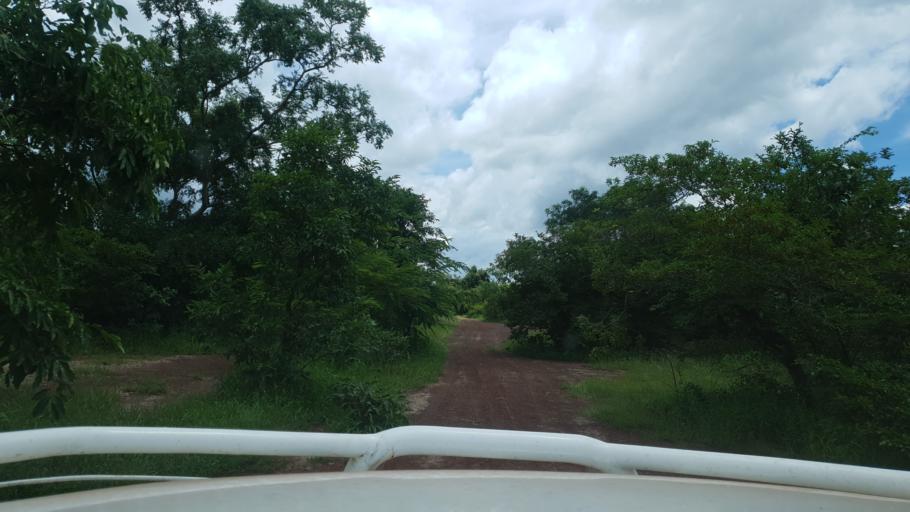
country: ML
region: Koulikoro
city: Banamba
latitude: 13.1957
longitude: -7.3232
